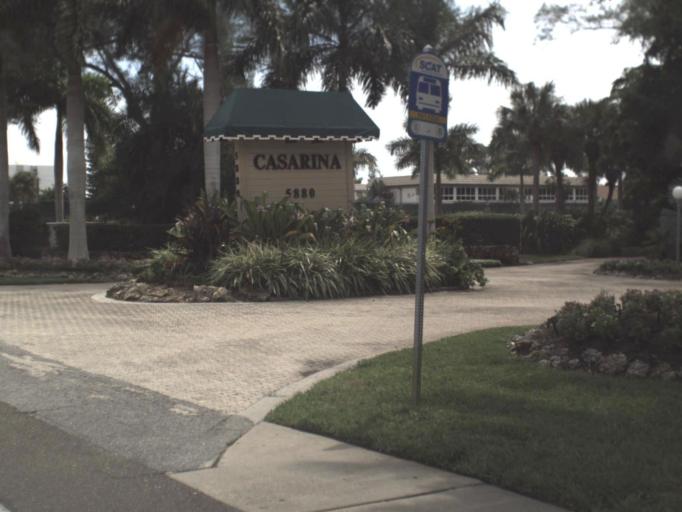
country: US
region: Florida
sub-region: Sarasota County
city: South Sarasota
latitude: 27.2640
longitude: -82.5423
